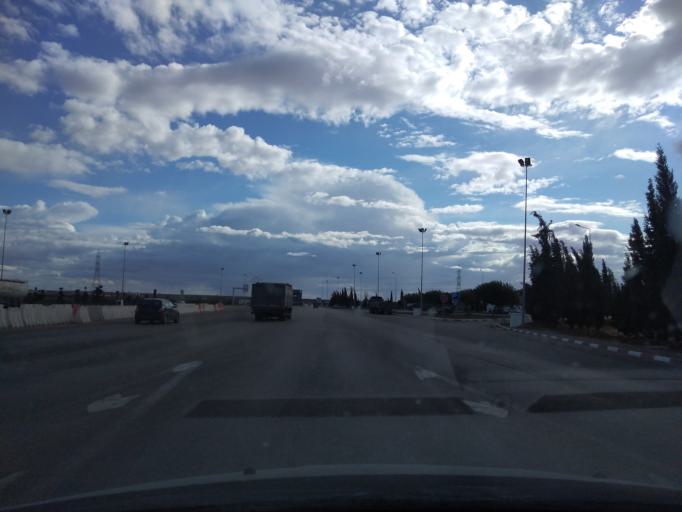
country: TN
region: Susah
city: Masakin
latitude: 35.6901
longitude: 10.5630
